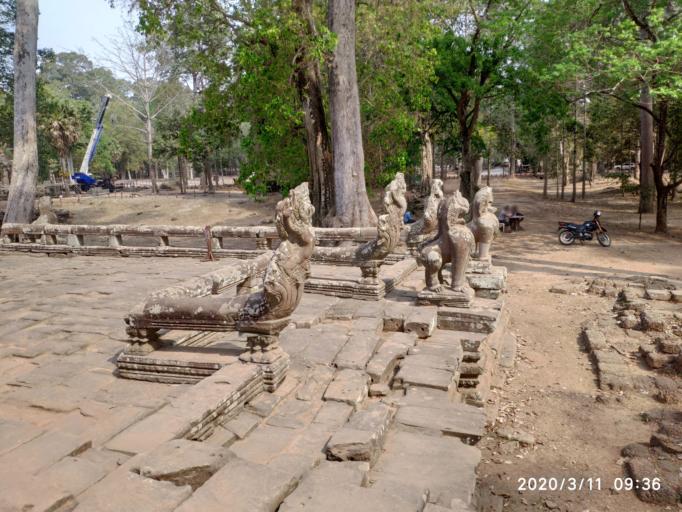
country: KH
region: Siem Reap
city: Siem Reap
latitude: 13.4413
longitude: 103.8602
